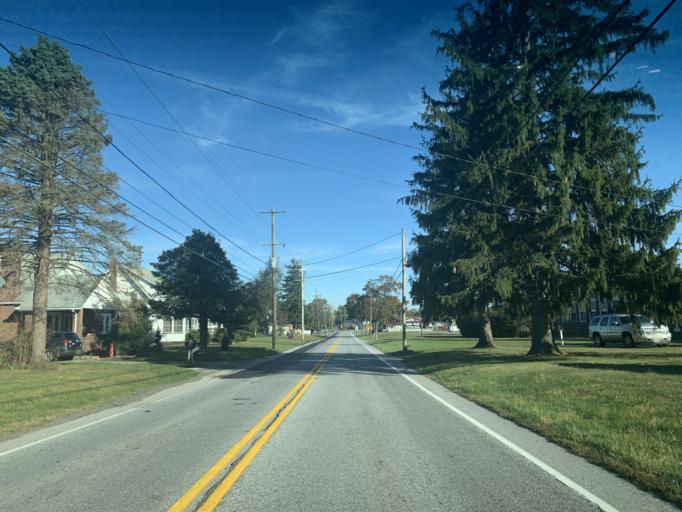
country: US
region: Pennsylvania
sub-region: Chester County
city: Parkesburg
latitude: 39.8880
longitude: -75.9229
